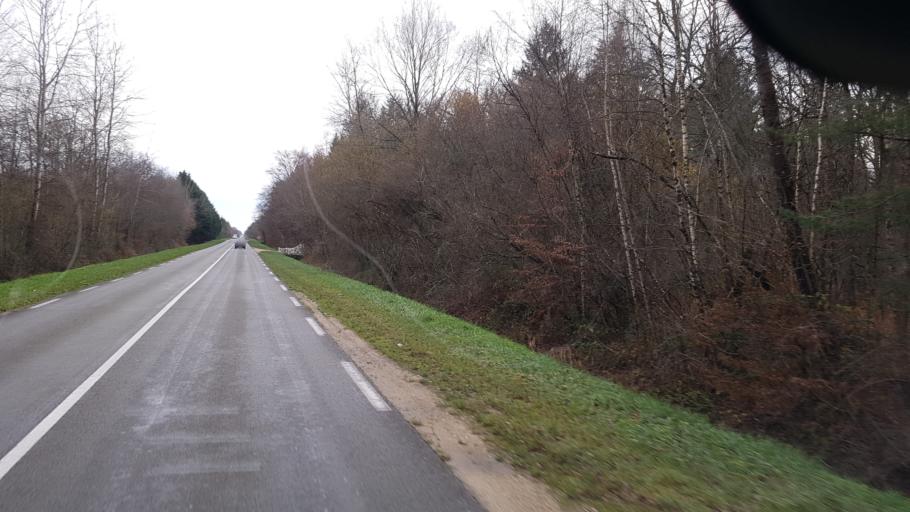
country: FR
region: Centre
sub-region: Departement du Loiret
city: La Ferte-Saint-Aubin
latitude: 47.6721
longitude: 1.9717
